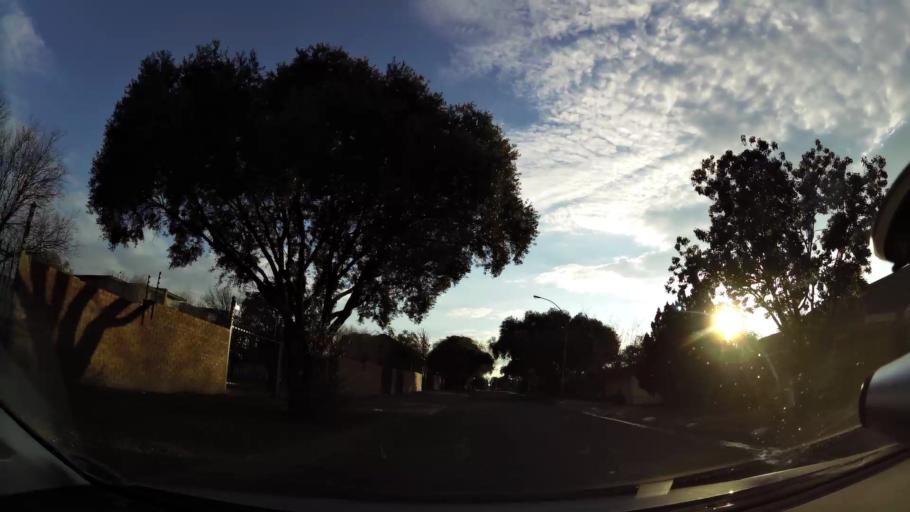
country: ZA
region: Orange Free State
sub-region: Mangaung Metropolitan Municipality
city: Bloemfontein
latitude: -29.1427
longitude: 26.1817
